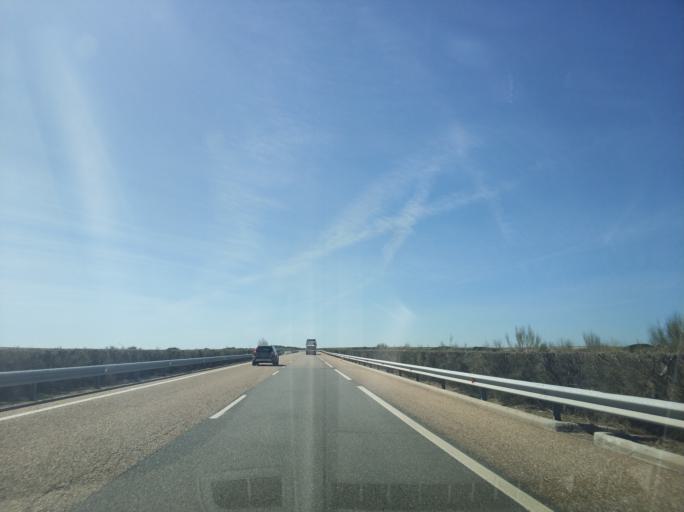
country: ES
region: Castille and Leon
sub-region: Provincia de Valladolid
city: Alaejos
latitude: 41.2811
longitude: -5.2486
